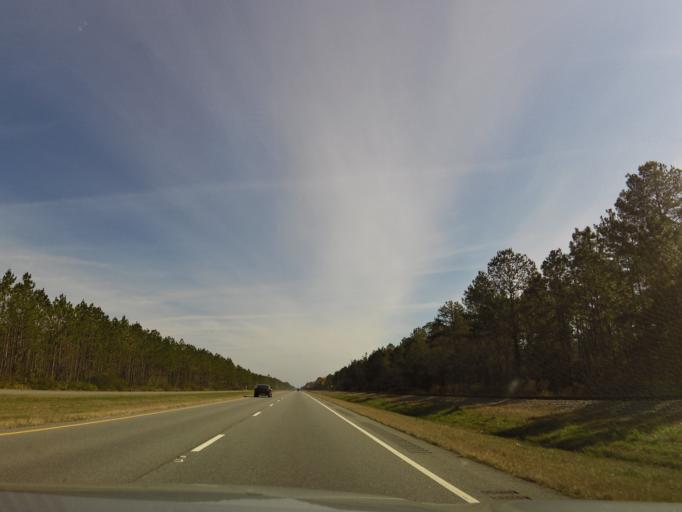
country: US
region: Georgia
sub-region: Lowndes County
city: Valdosta
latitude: 30.8765
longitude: -83.1597
